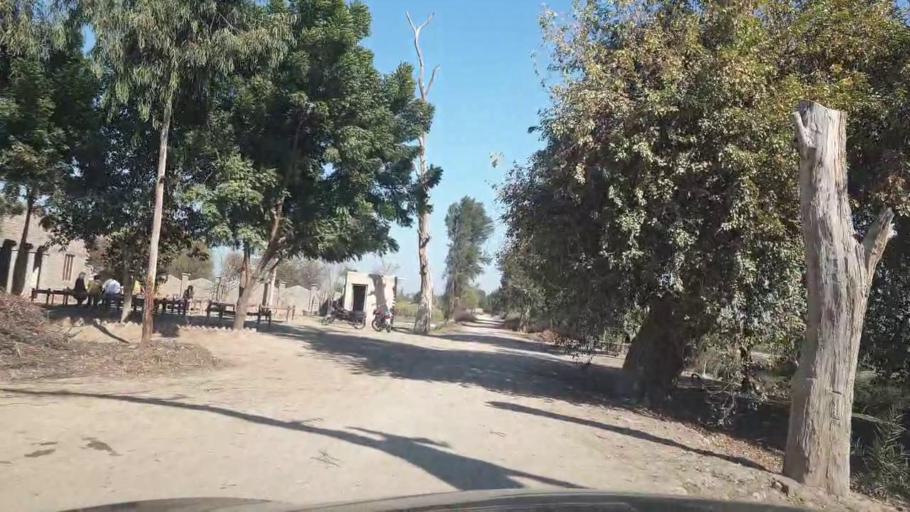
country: PK
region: Sindh
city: Ghotki
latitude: 27.9782
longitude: 69.4201
